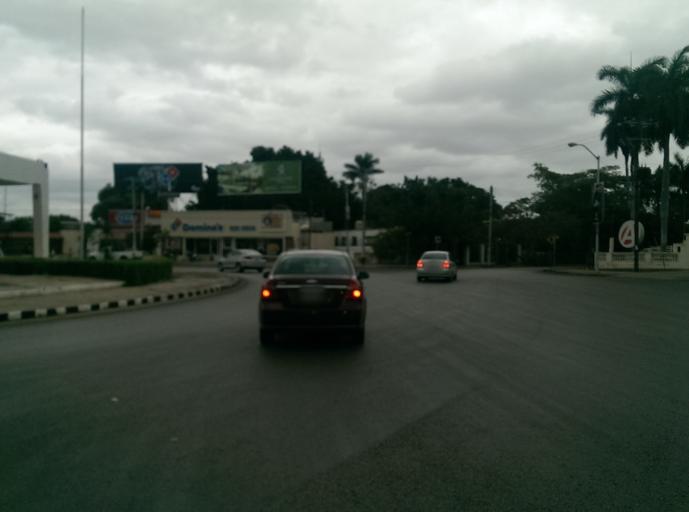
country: MX
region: Yucatan
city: Merida
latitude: 20.9884
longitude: -89.6388
